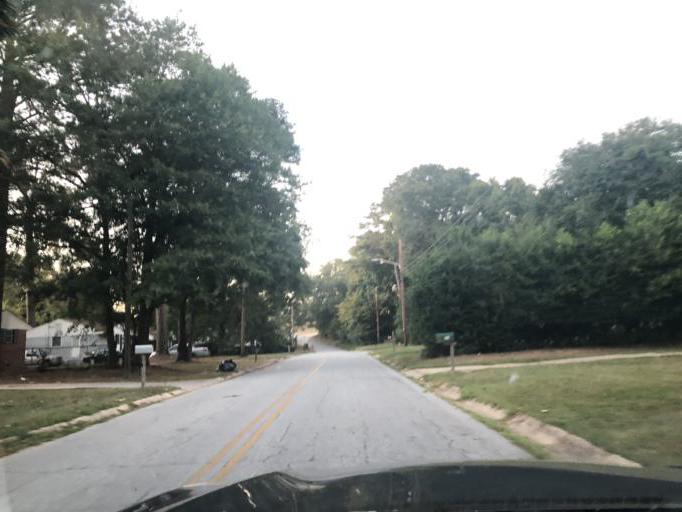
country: US
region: Georgia
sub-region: Muscogee County
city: Columbus
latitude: 32.4735
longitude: -84.8994
